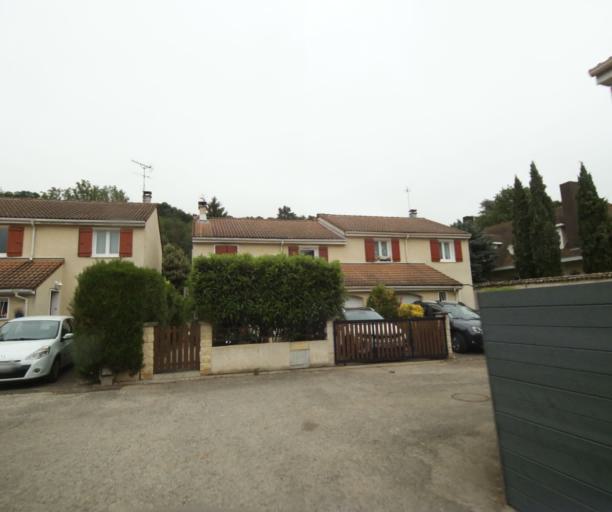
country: FR
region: Rhone-Alpes
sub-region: Departement de l'Ain
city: Miribel
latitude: 45.8280
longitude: 4.9594
